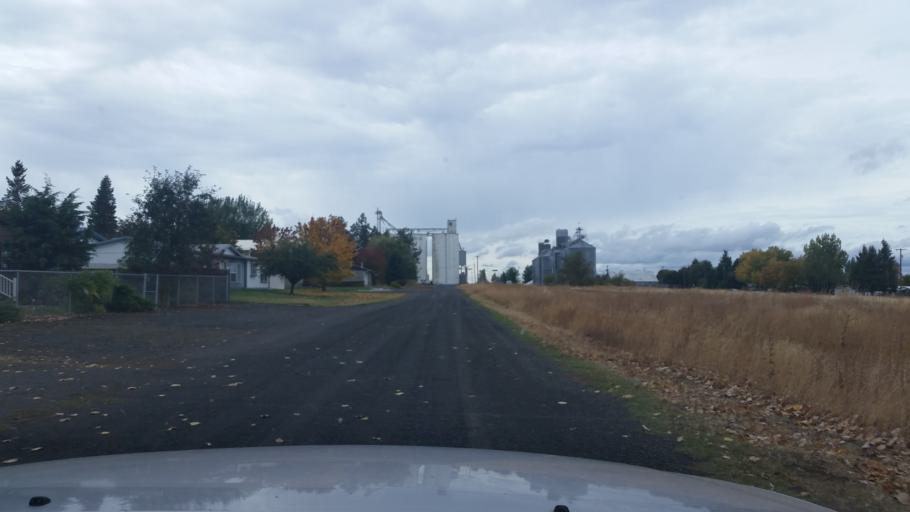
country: US
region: Washington
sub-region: Spokane County
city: Medical Lake
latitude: 47.6706
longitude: -117.8737
